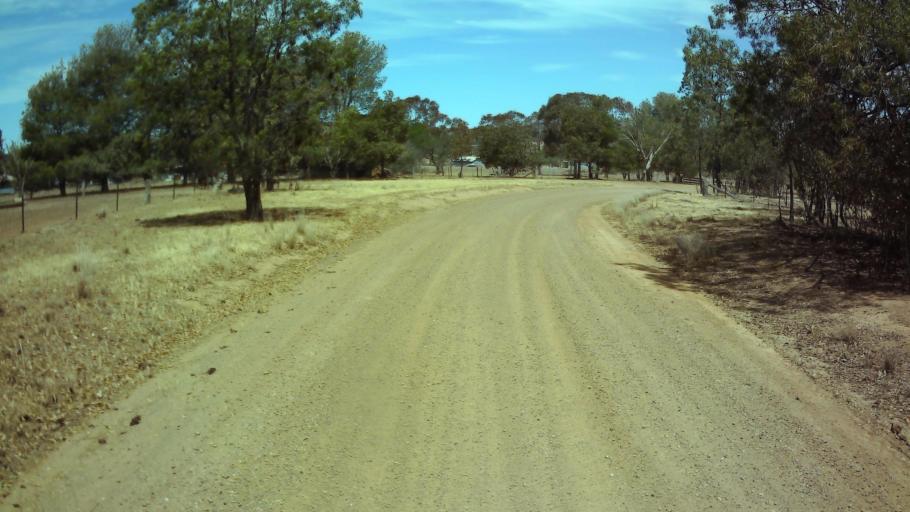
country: AU
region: New South Wales
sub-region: Weddin
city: Grenfell
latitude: -33.8293
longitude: 148.1750
